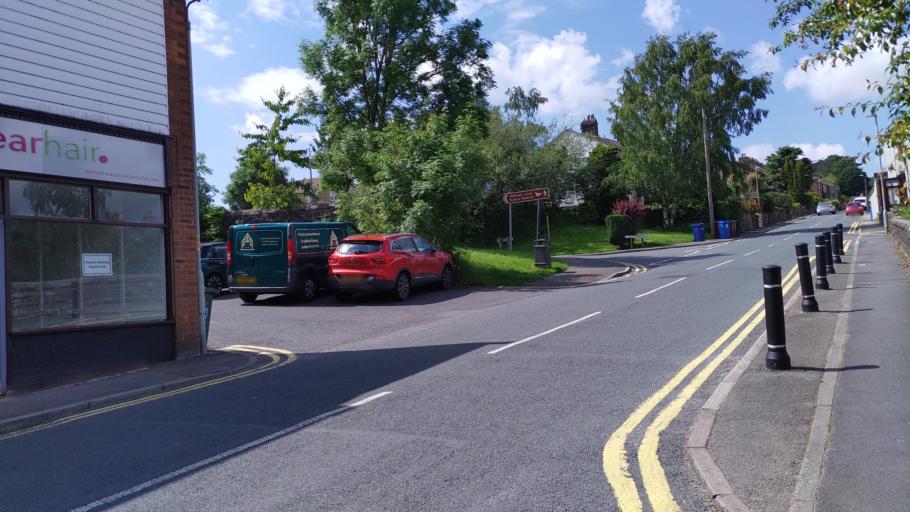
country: GB
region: England
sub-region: Lancashire
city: Chorley
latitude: 53.6935
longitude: -2.5567
